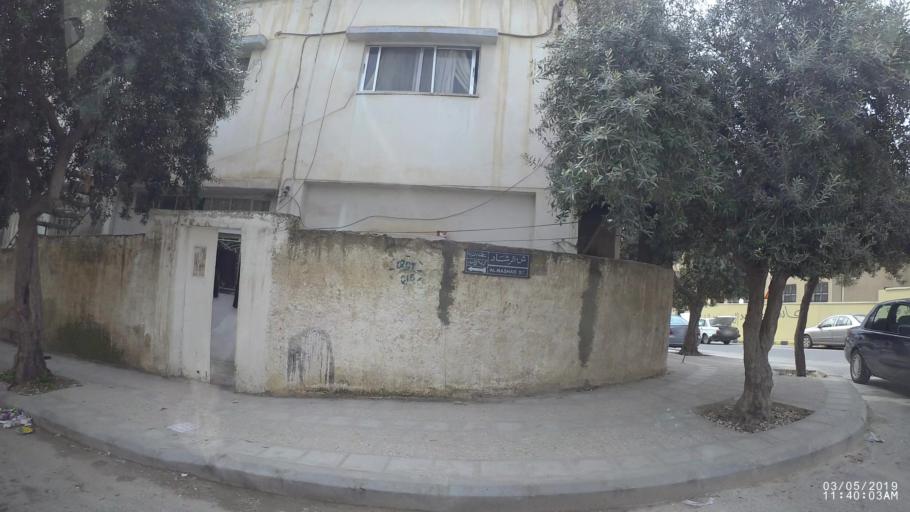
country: JO
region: Amman
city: Amman
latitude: 31.9632
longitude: 35.9535
